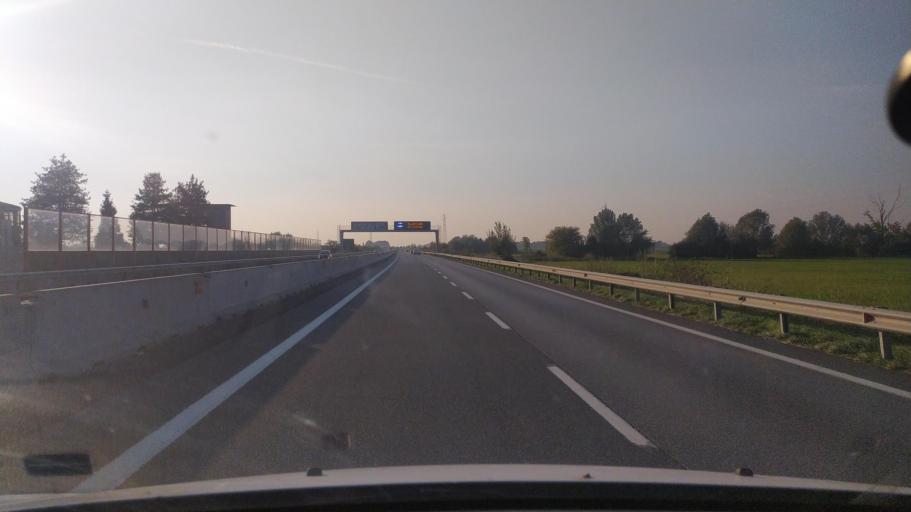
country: IT
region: Lombardy
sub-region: Provincia di Cremona
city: Nosadello
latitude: 45.3877
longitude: 9.5352
